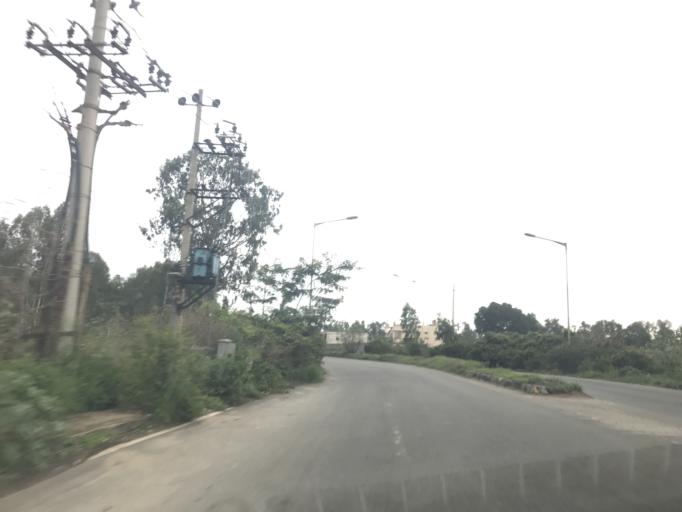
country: IN
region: Karnataka
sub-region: Bangalore Urban
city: Yelahanka
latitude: 13.1328
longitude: 77.6552
